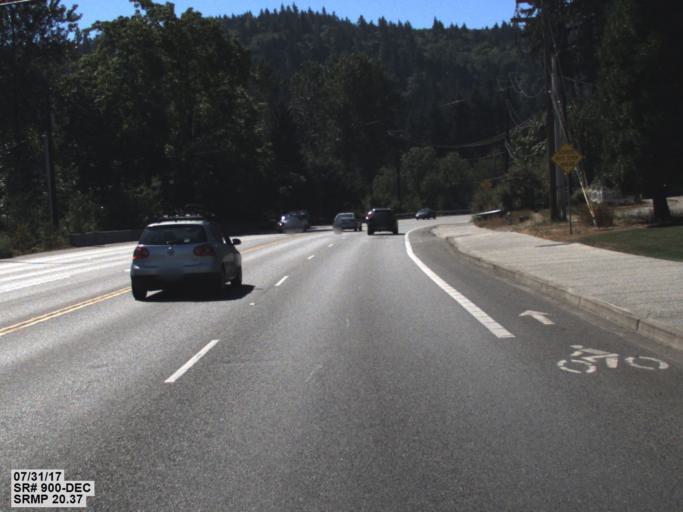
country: US
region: Washington
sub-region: King County
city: Issaquah
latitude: 47.5309
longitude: -122.0619
